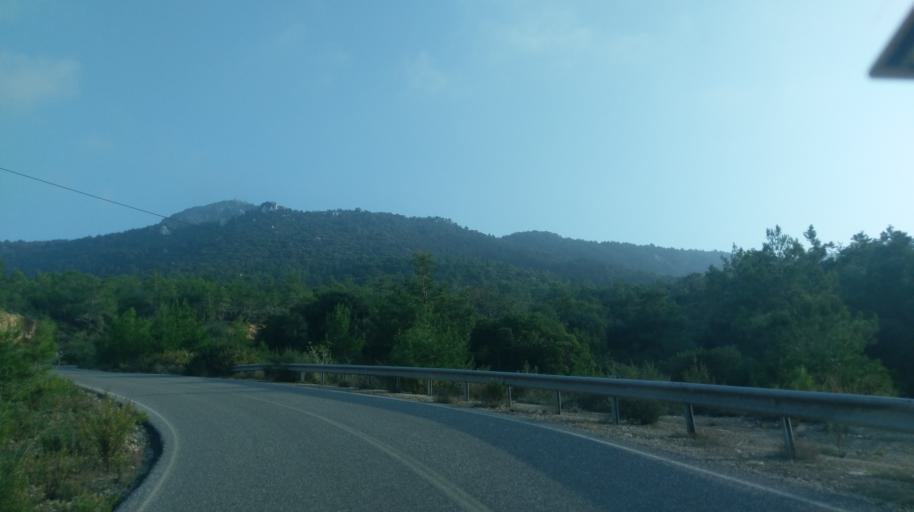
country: CY
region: Ammochostos
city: Trikomo
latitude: 35.4103
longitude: 33.9045
